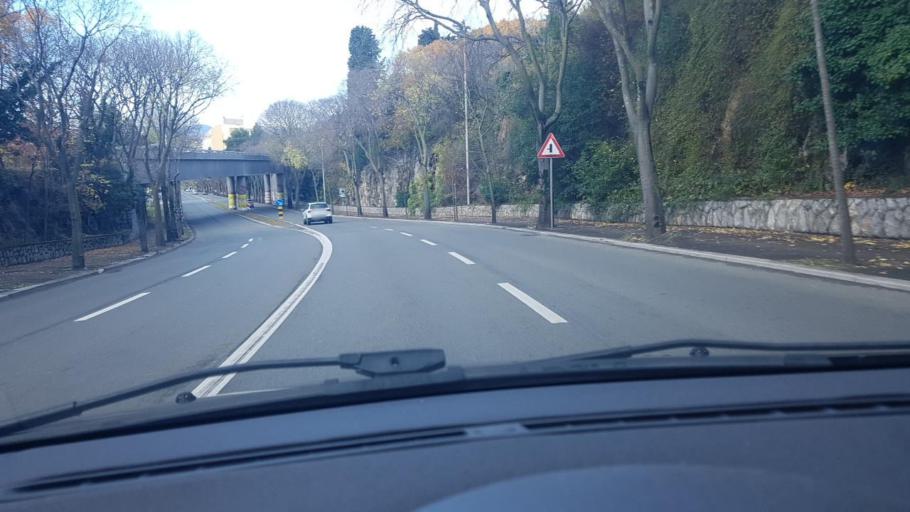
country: HR
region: Primorsko-Goranska
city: Rijeka
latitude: 45.3391
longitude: 14.3976
